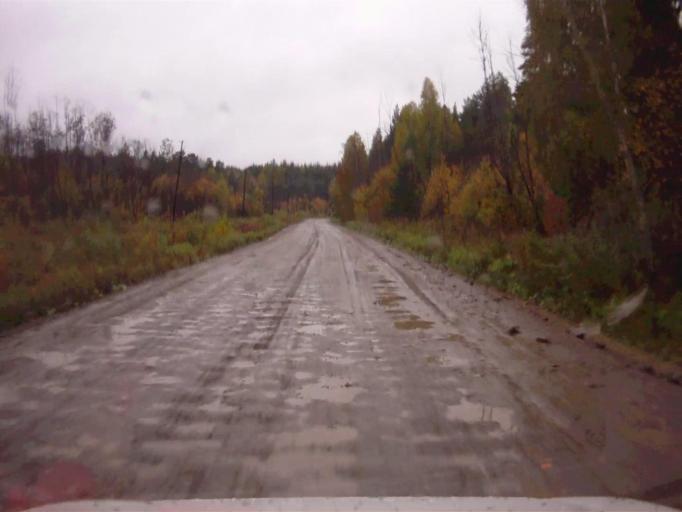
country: RU
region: Chelyabinsk
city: Kyshtym
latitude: 55.7424
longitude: 60.5024
